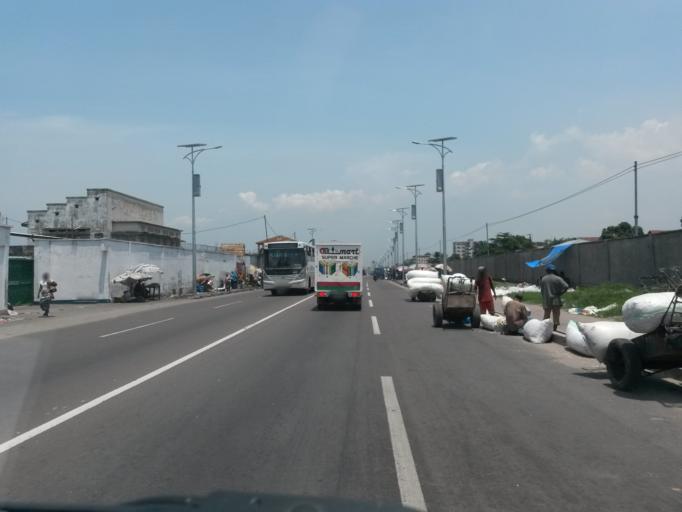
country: CD
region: Kinshasa
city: Kinshasa
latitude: -4.3115
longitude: 15.3311
